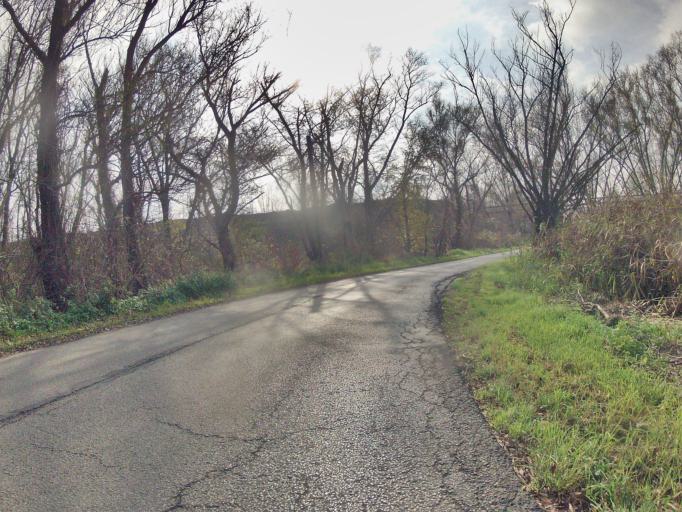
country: PL
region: Lesser Poland Voivodeship
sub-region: Powiat wielicki
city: Wegrzce Wielkie
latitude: 50.0655
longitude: 20.1096
